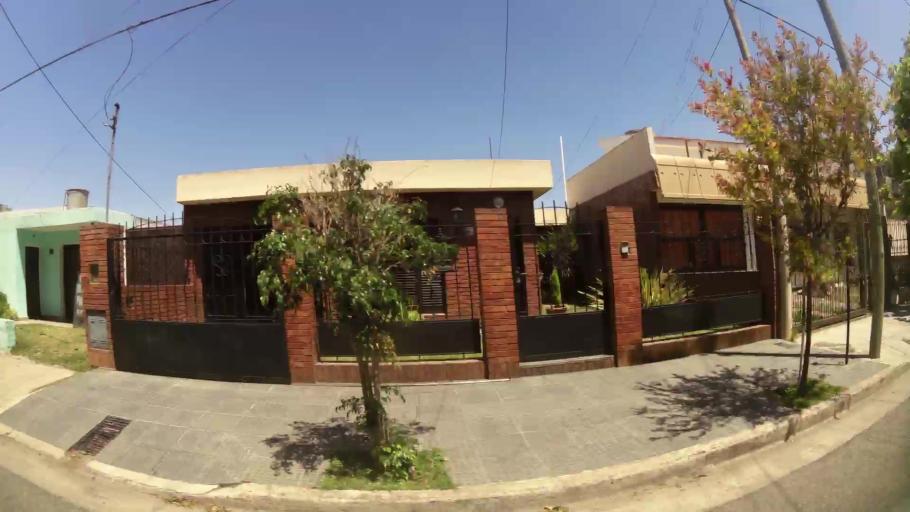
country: AR
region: Cordoba
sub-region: Departamento de Capital
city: Cordoba
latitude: -31.3877
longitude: -64.1406
